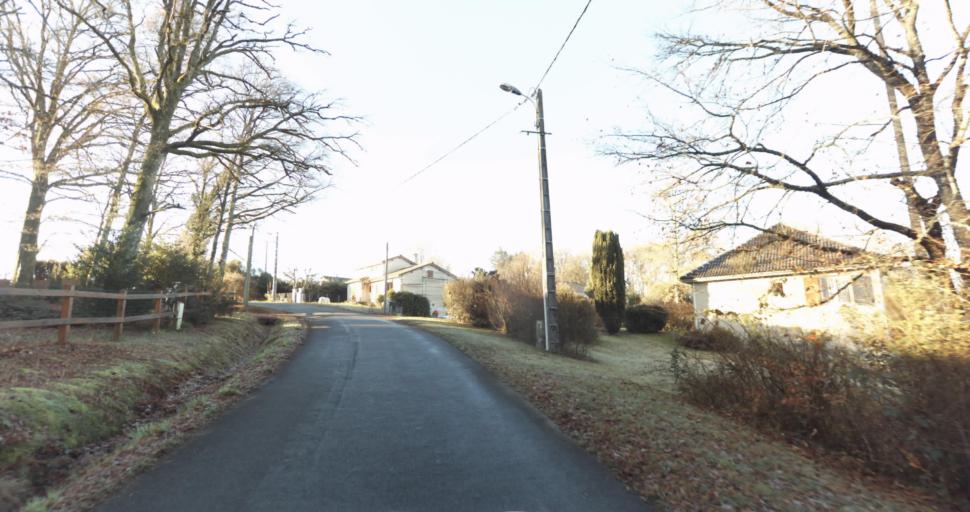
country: FR
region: Limousin
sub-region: Departement de la Haute-Vienne
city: Aixe-sur-Vienne
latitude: 45.8169
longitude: 1.1517
